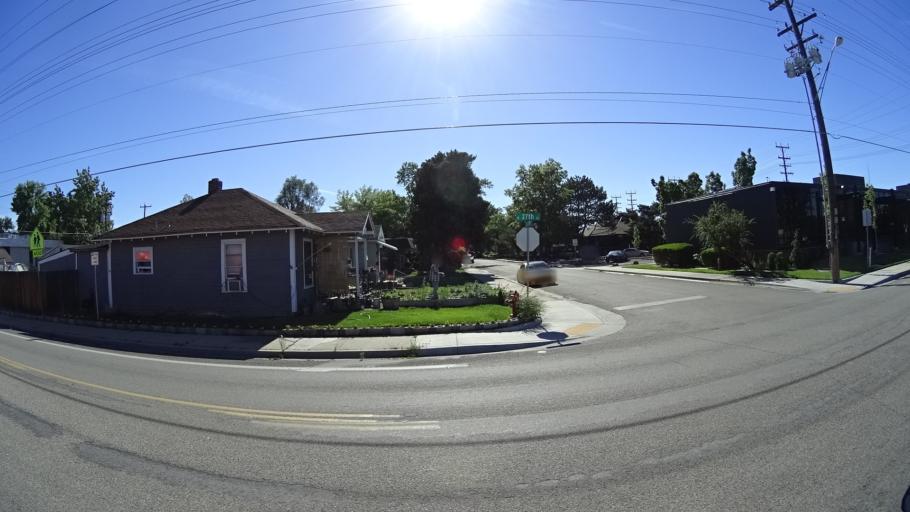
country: US
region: Idaho
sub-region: Ada County
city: Garden City
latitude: 43.6229
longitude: -116.2240
